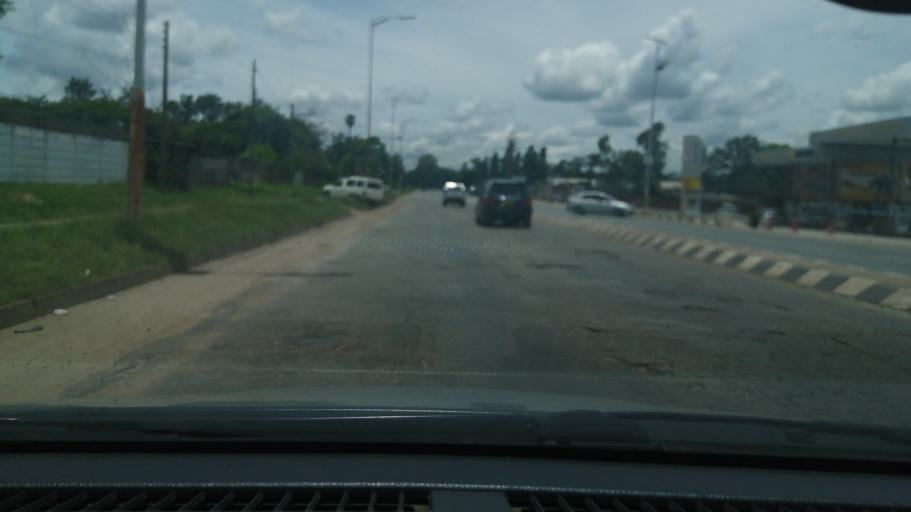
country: ZW
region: Harare
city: Harare
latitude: -17.8738
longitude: 31.0656
